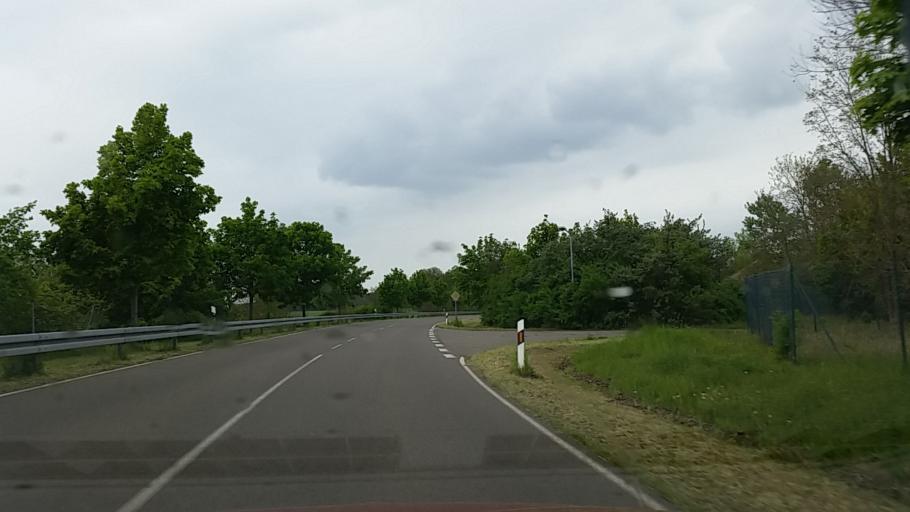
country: DE
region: Brandenburg
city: Rauen
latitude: 52.3194
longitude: 13.9542
